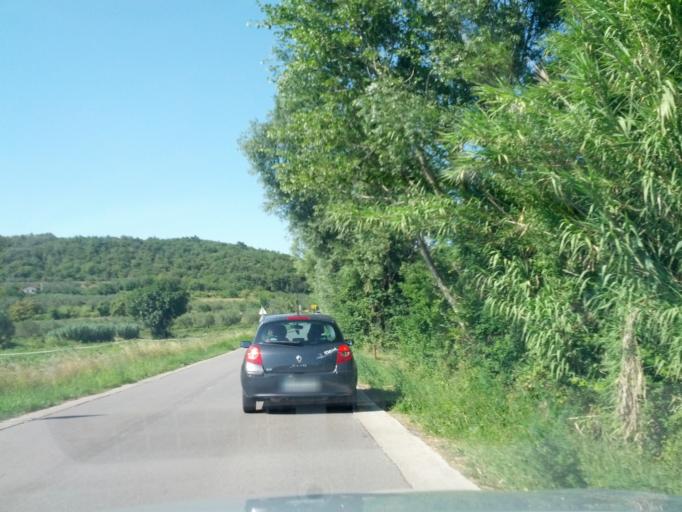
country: SI
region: Koper-Capodistria
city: Hrvatini
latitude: 45.5677
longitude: 13.7588
